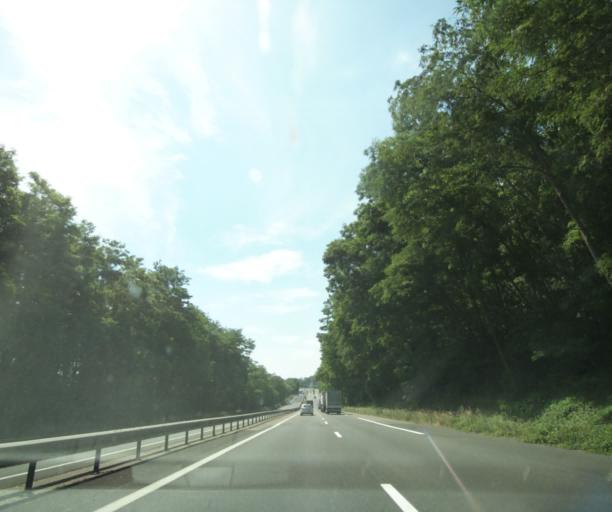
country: FR
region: Lorraine
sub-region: Departement de Meurthe-et-Moselle
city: Rosieres-aux-Salines
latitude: 48.6090
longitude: 6.3312
